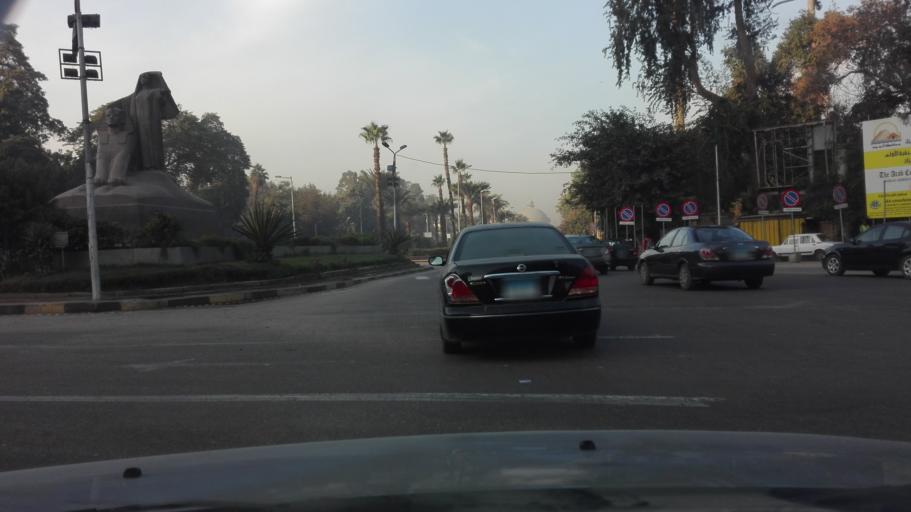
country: EG
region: Al Jizah
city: Al Jizah
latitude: 30.0288
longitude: 31.2162
